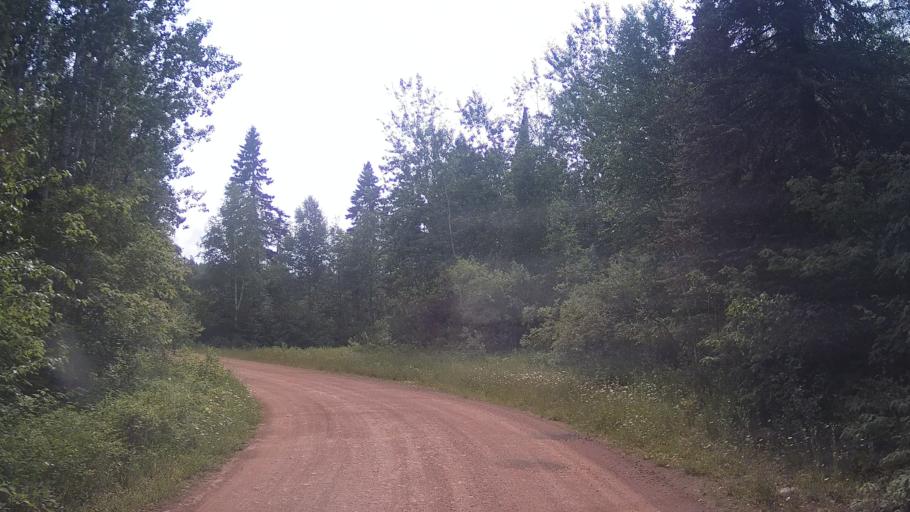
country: CA
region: Ontario
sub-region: Thunder Bay District
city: Thunder Bay
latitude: 48.6790
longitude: -88.6682
